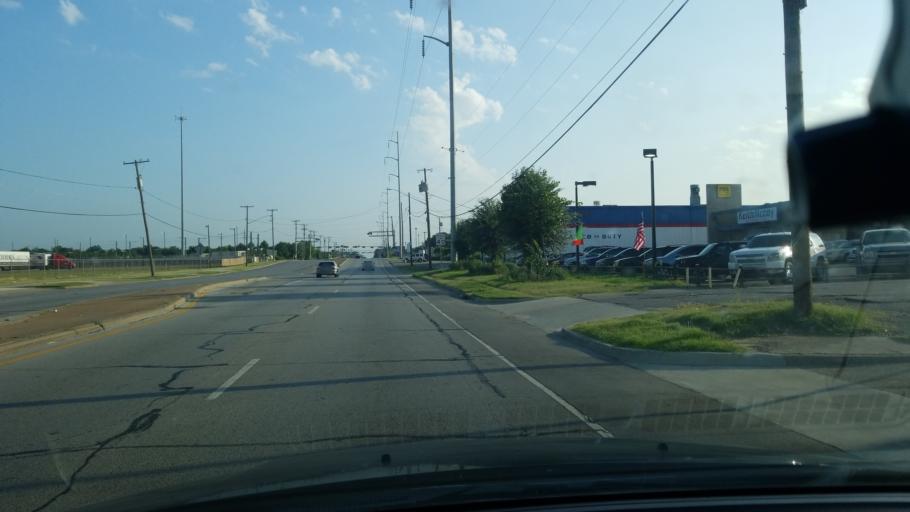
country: US
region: Texas
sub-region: Dallas County
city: Balch Springs
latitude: 32.7151
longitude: -96.6829
